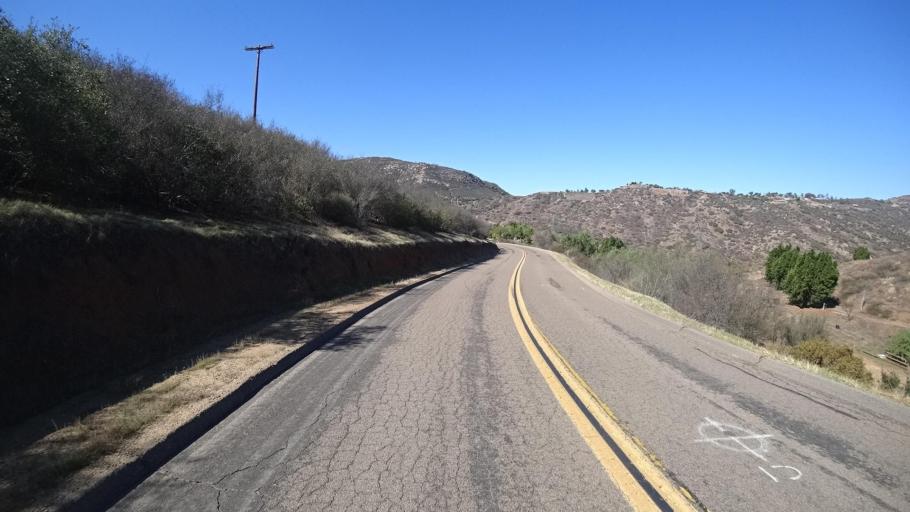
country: US
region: California
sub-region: San Diego County
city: Alpine
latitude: 32.8537
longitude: -116.7988
